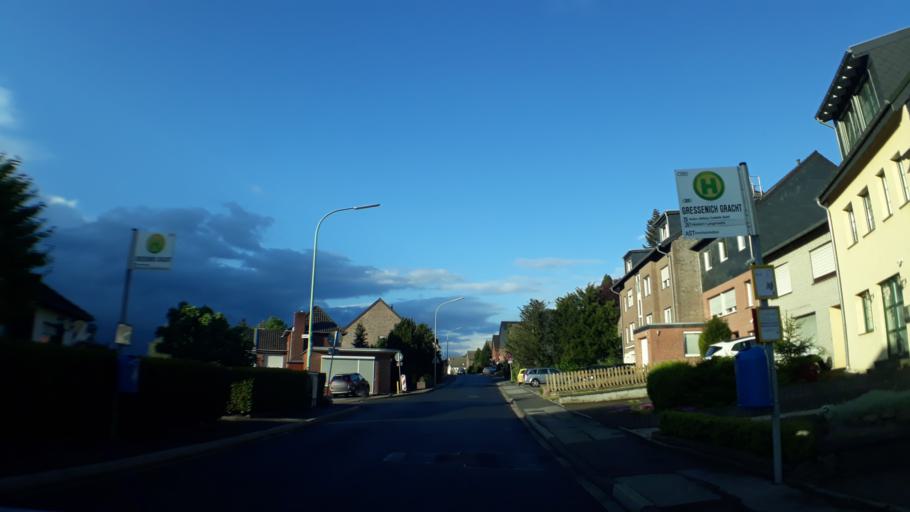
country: DE
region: North Rhine-Westphalia
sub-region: Regierungsbezirk Koln
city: Eschweiler
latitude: 50.7727
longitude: 6.3069
